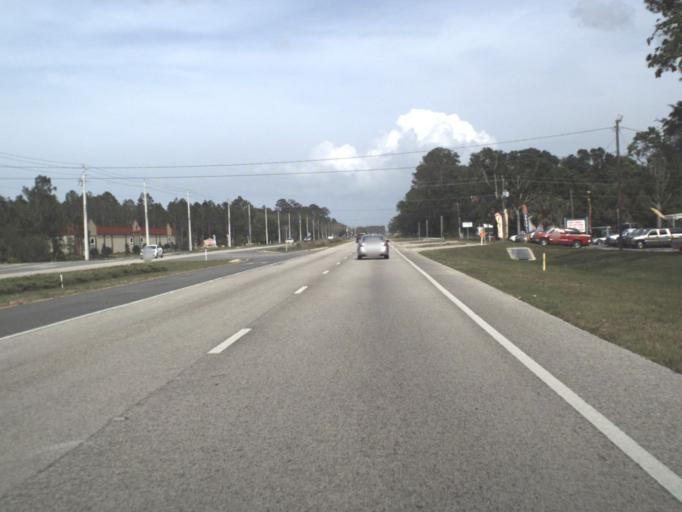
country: US
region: Florida
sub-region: Flagler County
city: Bunnell
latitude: 29.4754
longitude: -81.2358
